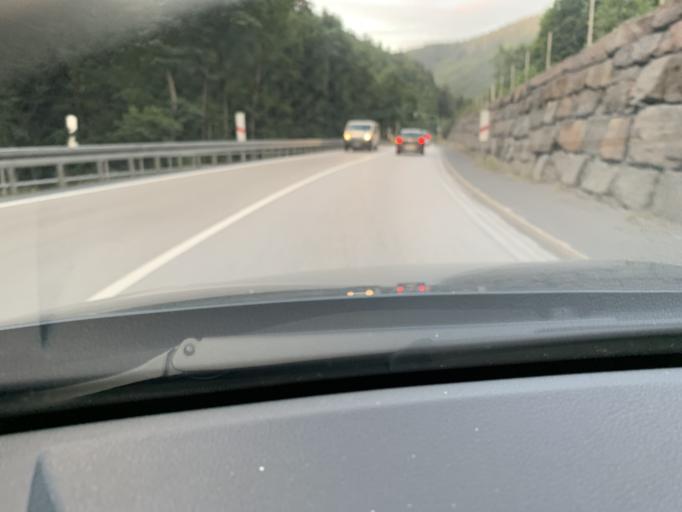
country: DE
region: Thuringia
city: Judenbach
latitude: 50.3867
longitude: 11.2002
